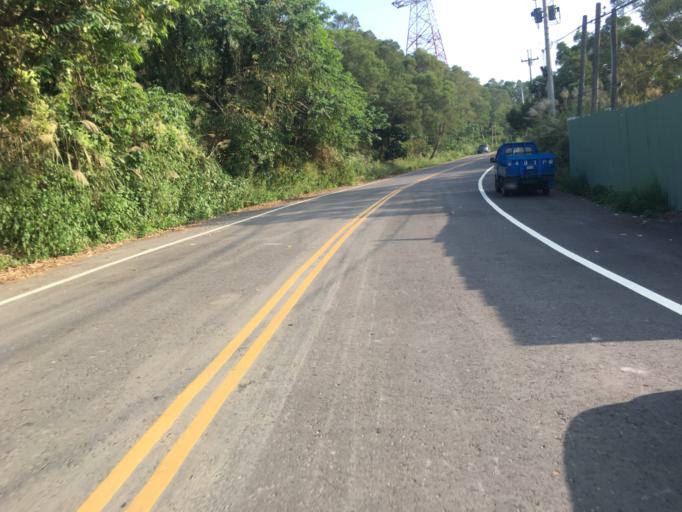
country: TW
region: Taiwan
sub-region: Hsinchu
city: Hsinchu
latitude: 24.7562
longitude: 121.0288
